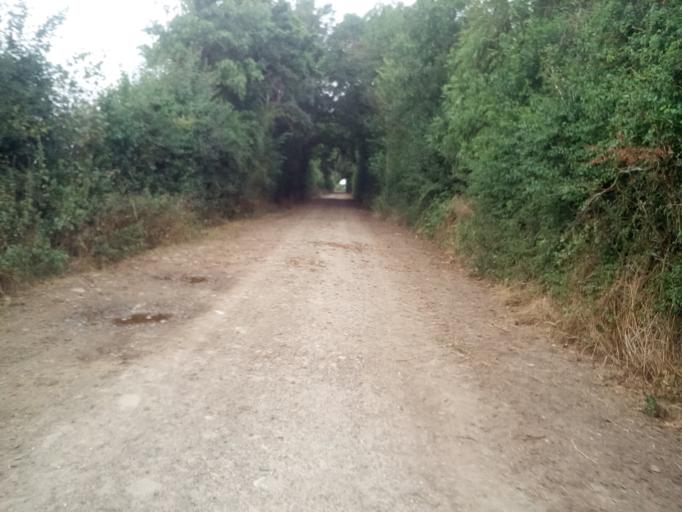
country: FR
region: Lower Normandy
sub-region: Departement du Calvados
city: Clinchamps-sur-Orne
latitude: 49.0454
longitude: -0.4008
